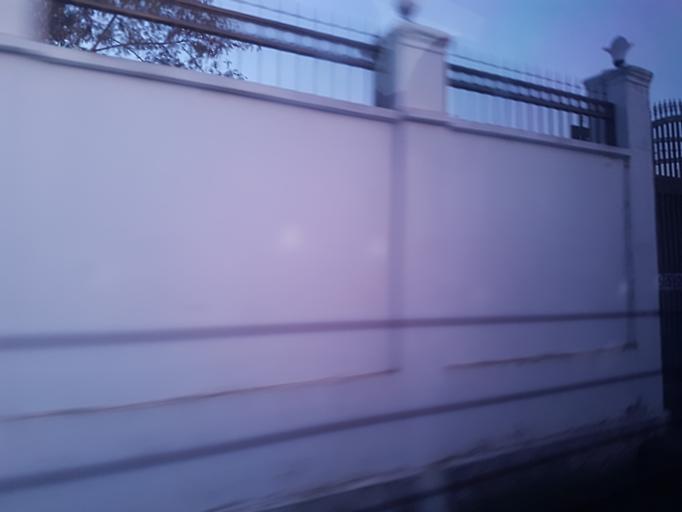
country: MM
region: Yangon
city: Yangon
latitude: 16.8049
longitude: 96.1654
